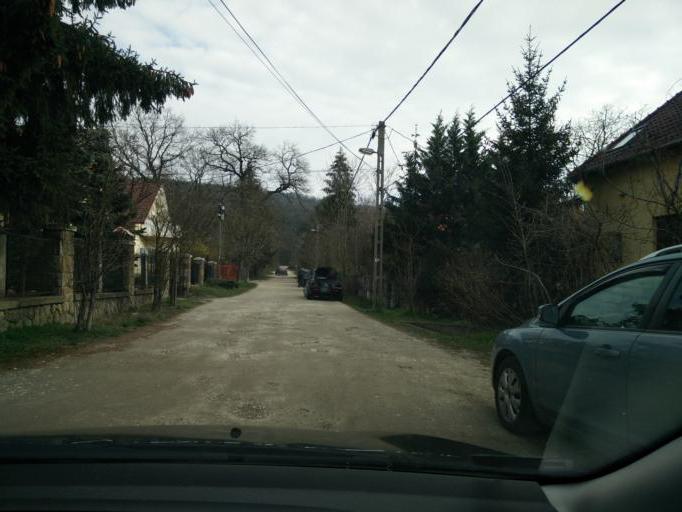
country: HU
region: Pest
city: Piliscsaba
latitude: 47.6380
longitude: 18.8459
